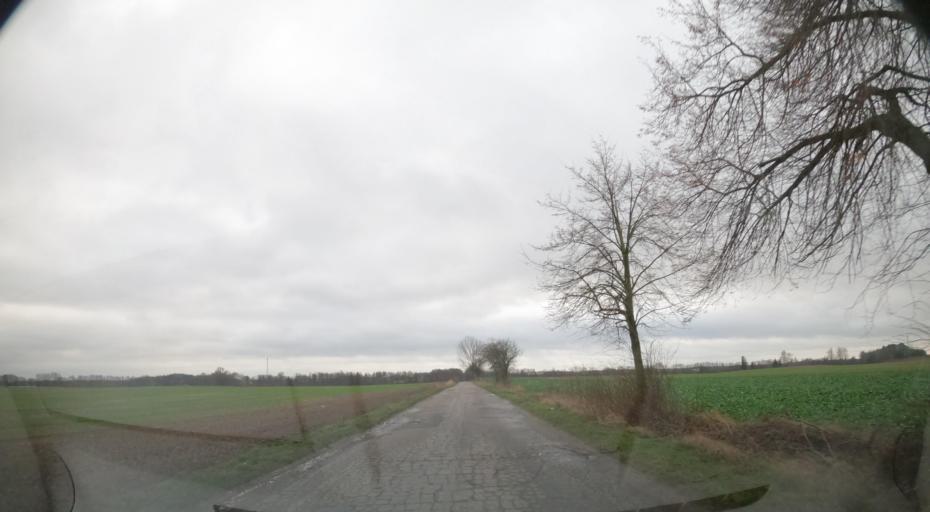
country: PL
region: Greater Poland Voivodeship
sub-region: Powiat pilski
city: Wysoka
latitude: 53.2619
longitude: 17.1144
